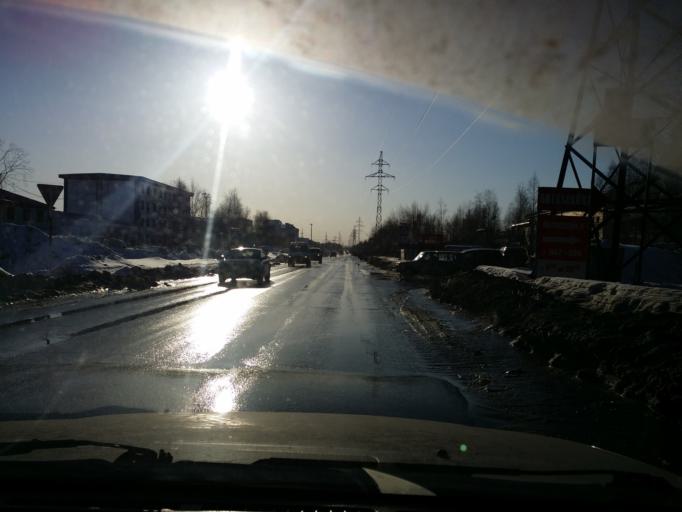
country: RU
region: Khanty-Mansiyskiy Avtonomnyy Okrug
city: Nizhnevartovsk
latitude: 60.9334
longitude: 76.5440
